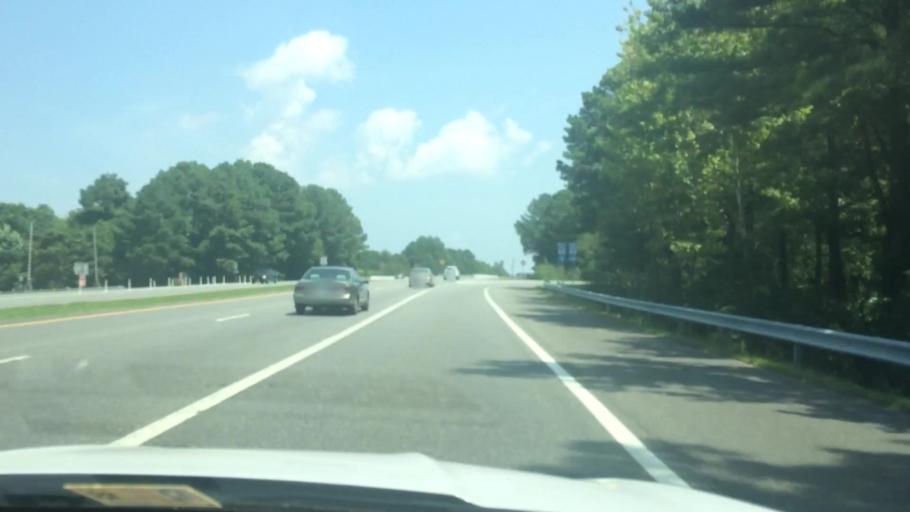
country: US
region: Virginia
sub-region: James City County
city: Williamsburg
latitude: 37.3516
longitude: -76.7340
